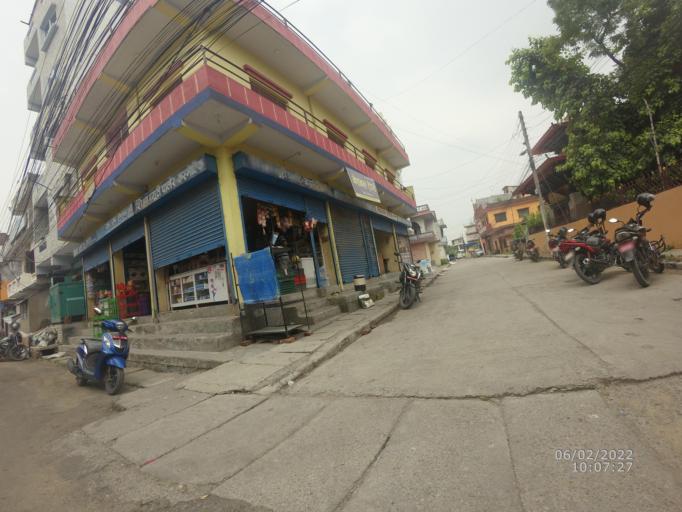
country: NP
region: Western Region
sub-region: Lumbini Zone
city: Bhairahawa
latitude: 27.5081
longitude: 83.4533
